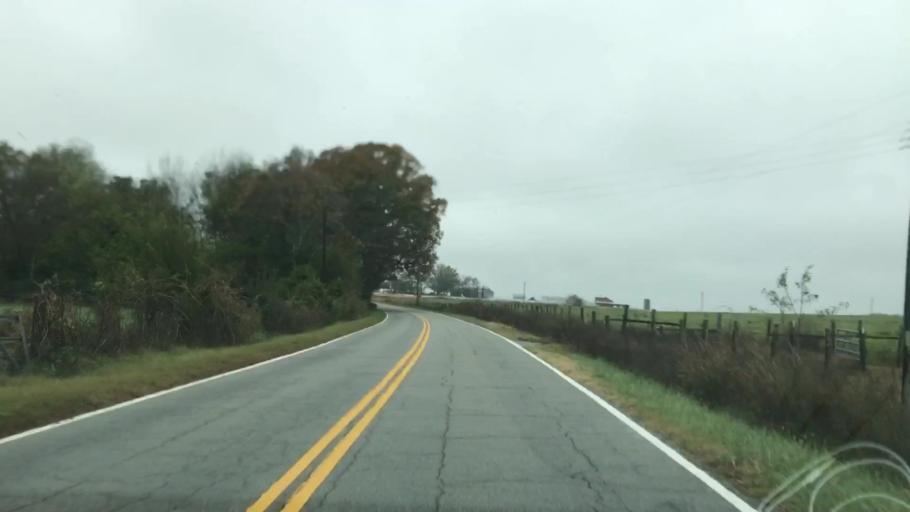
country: US
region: South Carolina
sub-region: Laurens County
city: Joanna
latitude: 34.3566
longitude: -81.7984
